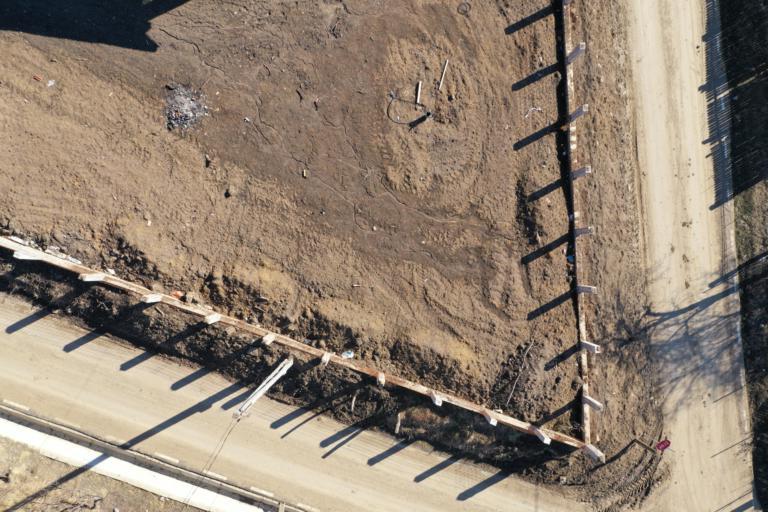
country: RO
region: Iasi
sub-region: Comuna Tibana
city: Tibana
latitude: 46.9853
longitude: 27.3534
